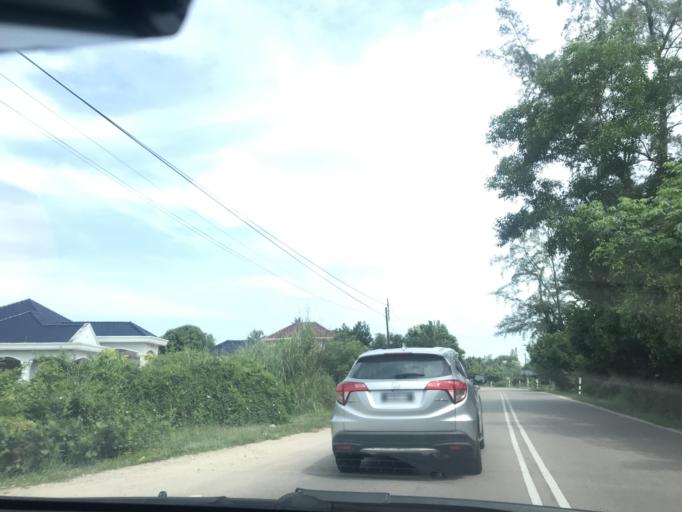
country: MY
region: Kelantan
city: Tumpat
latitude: 6.2158
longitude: 102.1245
